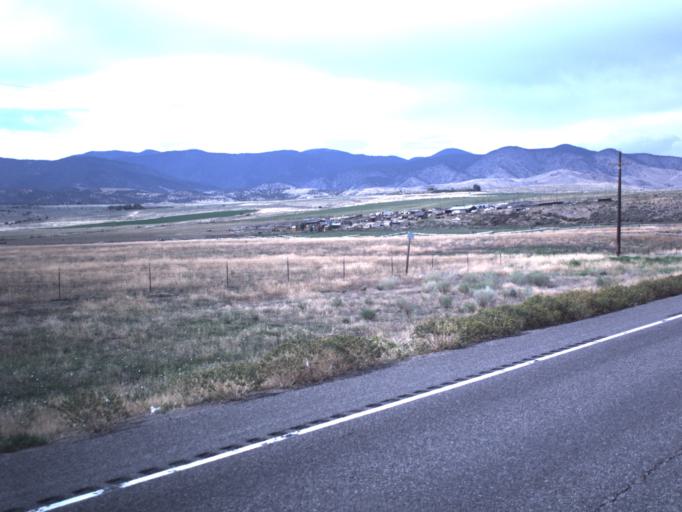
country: US
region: Utah
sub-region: Piute County
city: Junction
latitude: 38.4066
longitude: -112.2312
